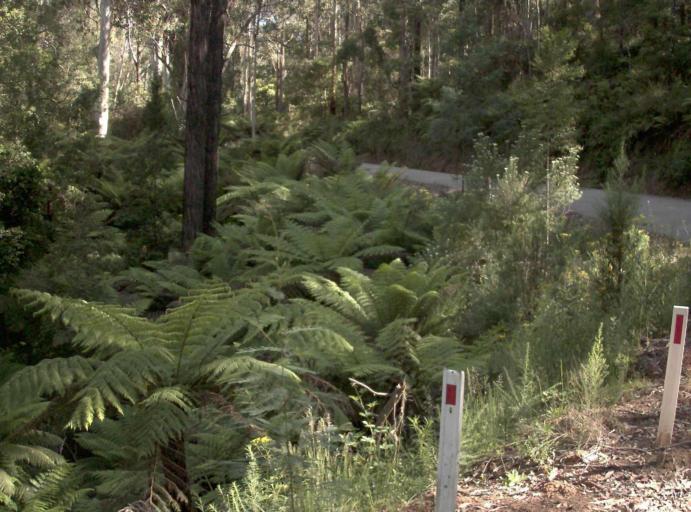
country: AU
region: Victoria
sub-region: East Gippsland
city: Lakes Entrance
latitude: -37.4248
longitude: 148.6022
